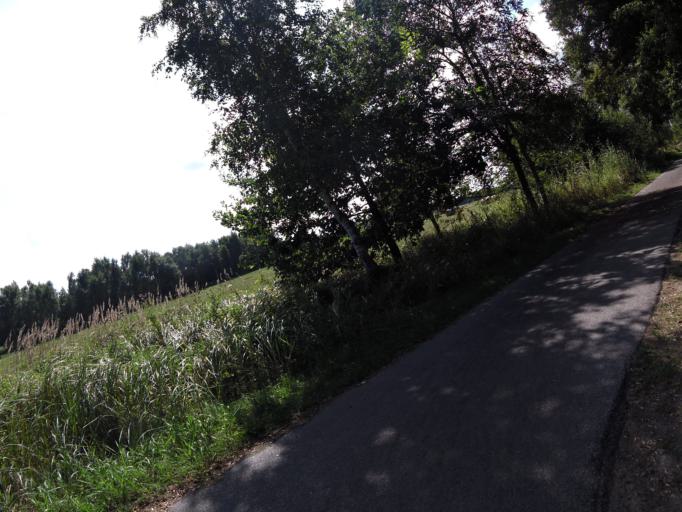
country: DE
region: Mecklenburg-Vorpommern
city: Kroslin
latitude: 54.1413
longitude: 13.7910
